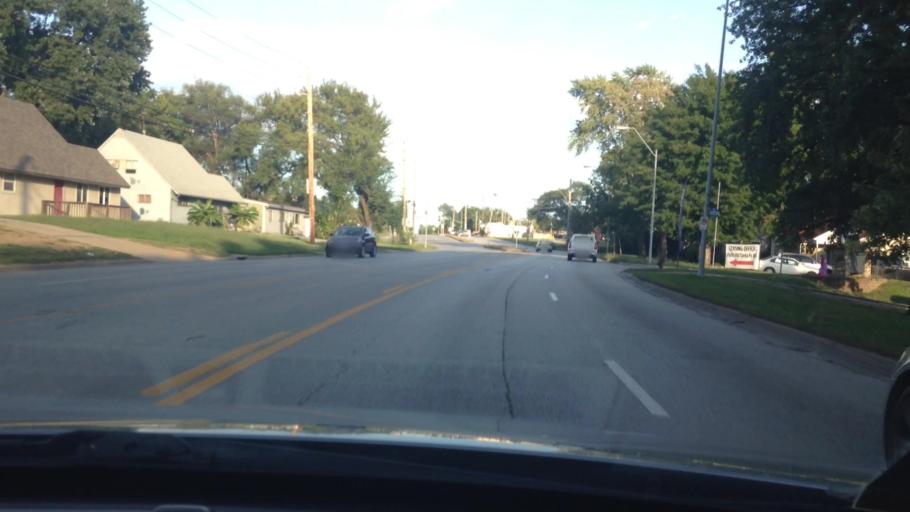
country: US
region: Missouri
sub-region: Jackson County
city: Raytown
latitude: 38.9667
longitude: -94.5032
